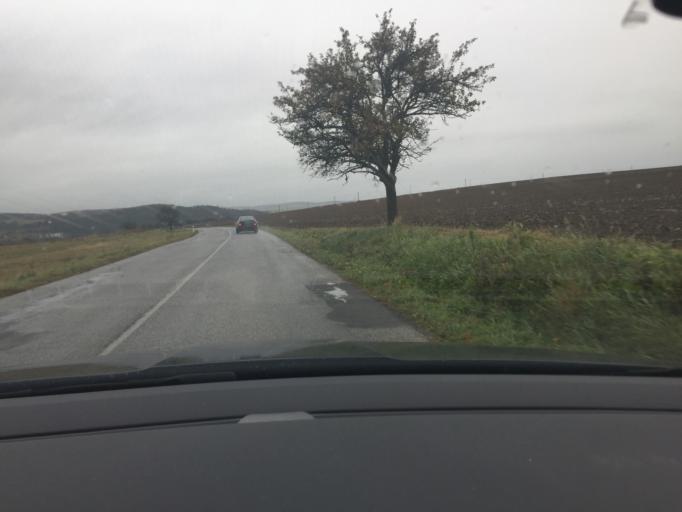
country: SK
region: Presovsky
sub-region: Okres Presov
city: Kezmarok
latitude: 49.1657
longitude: 20.4162
